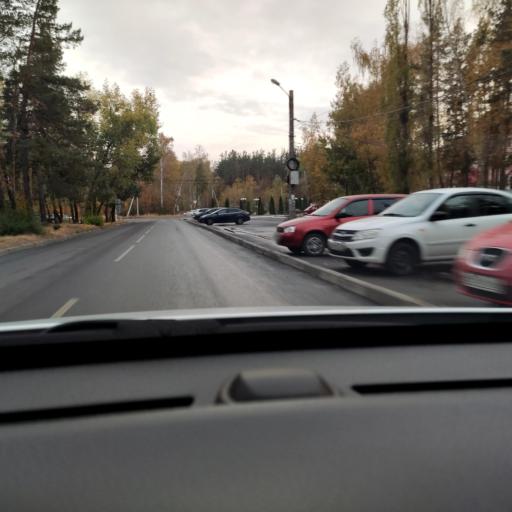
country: RU
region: Voronezj
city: Somovo
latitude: 51.6864
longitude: 39.2861
